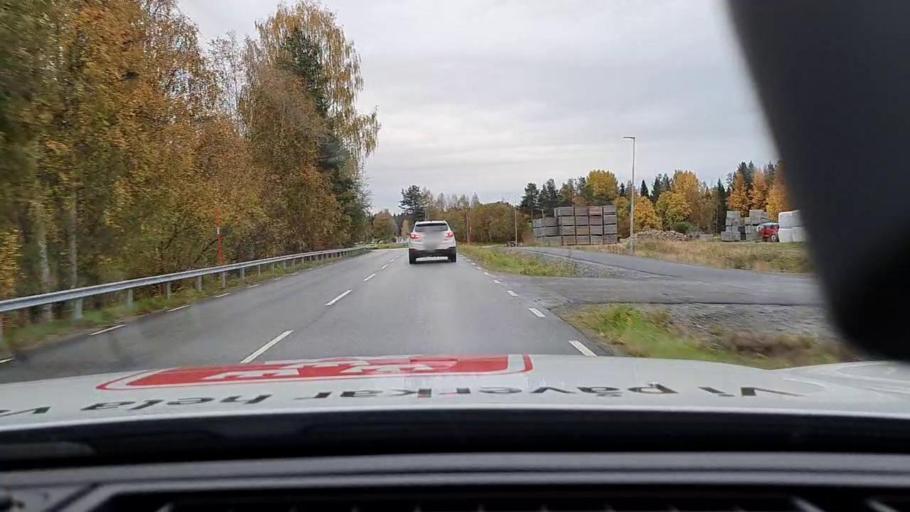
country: SE
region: Norrbotten
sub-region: Bodens Kommun
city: Saevast
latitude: 65.7696
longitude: 21.7061
